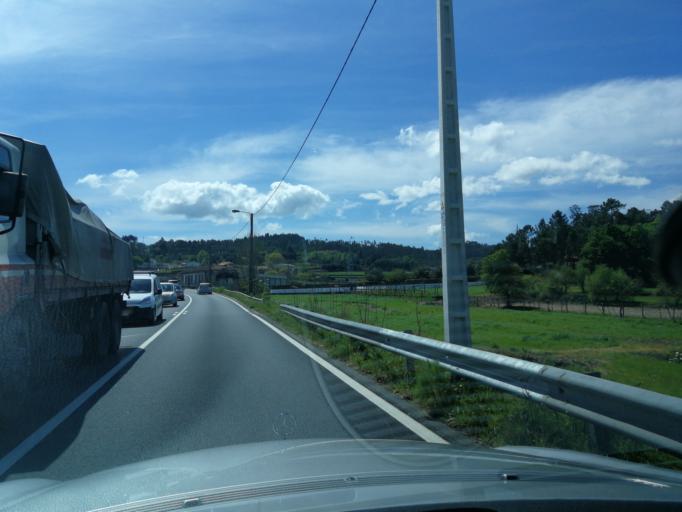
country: PT
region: Braga
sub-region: Vila Nova de Famalicao
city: Calendario
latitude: 41.4273
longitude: -8.5348
